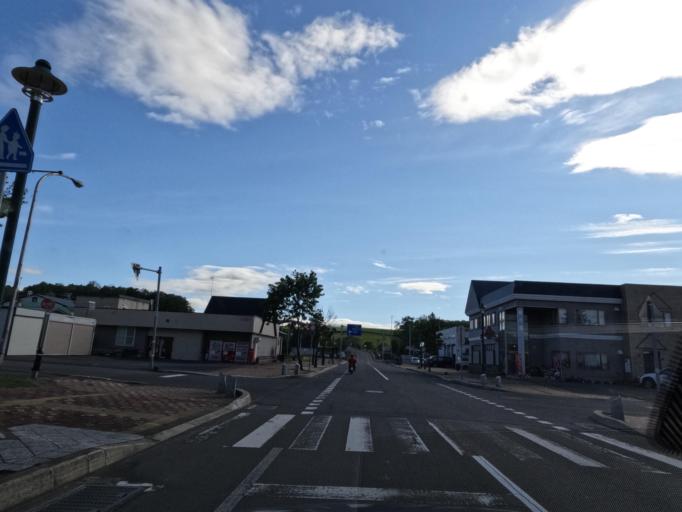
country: JP
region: Hokkaido
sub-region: Asahikawa-shi
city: Asahikawa
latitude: 43.5880
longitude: 142.4587
